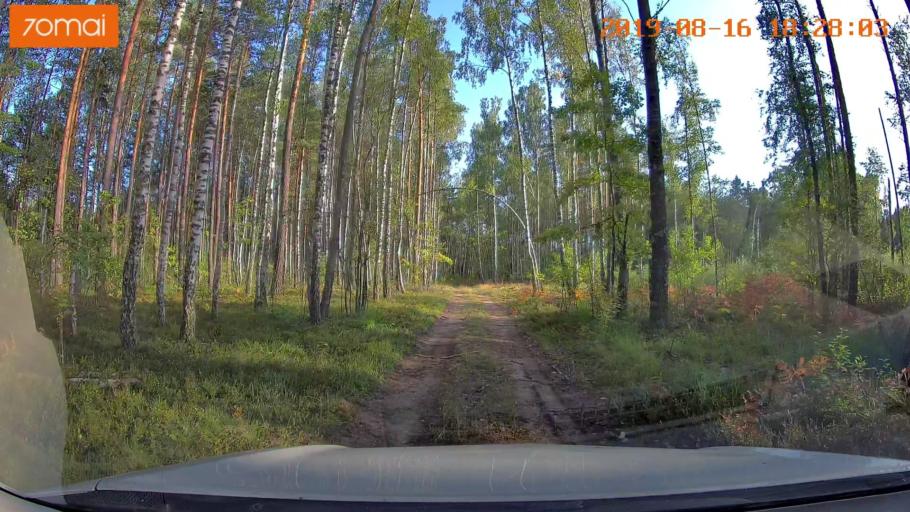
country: BY
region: Mogilev
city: Asipovichy
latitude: 53.2008
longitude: 28.6393
